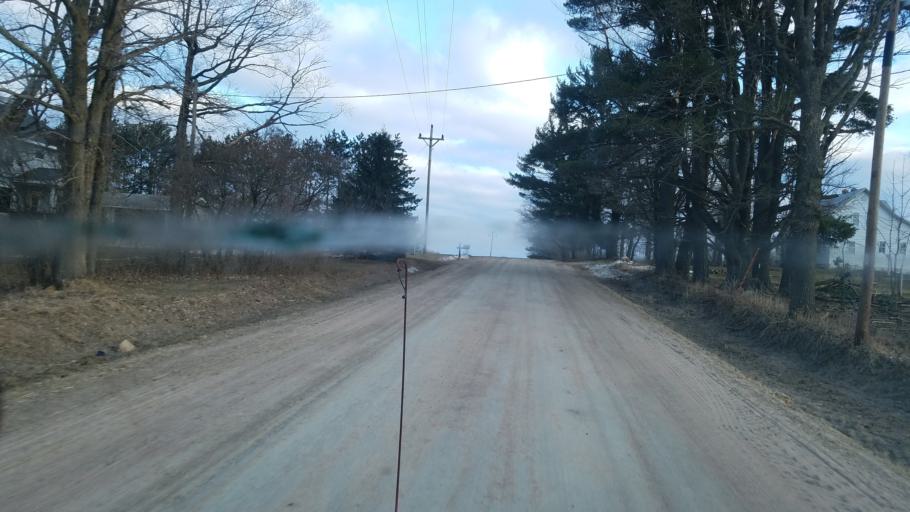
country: US
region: Wisconsin
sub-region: Clark County
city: Loyal
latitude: 44.6226
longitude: -90.4360
